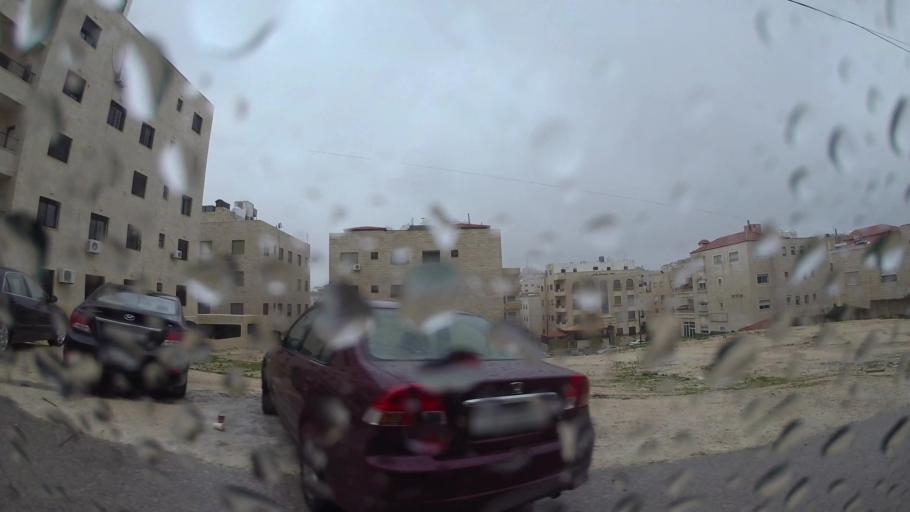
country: JO
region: Amman
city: Al Jubayhah
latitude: 32.0219
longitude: 35.8841
